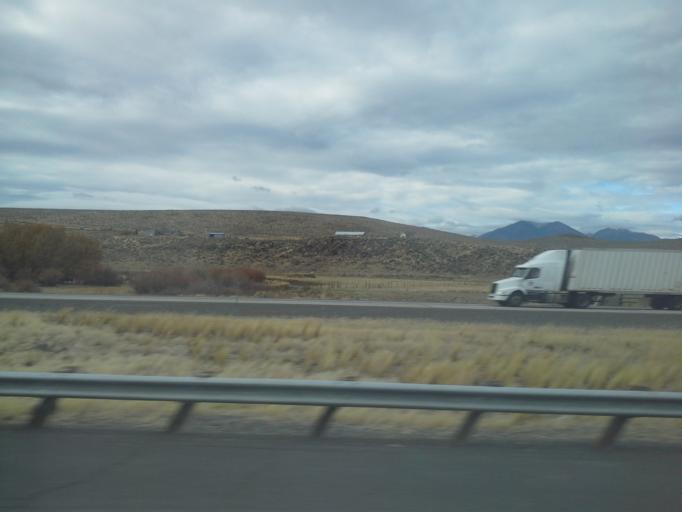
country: US
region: Oregon
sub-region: Baker County
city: Baker City
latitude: 44.9819
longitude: -117.8899
